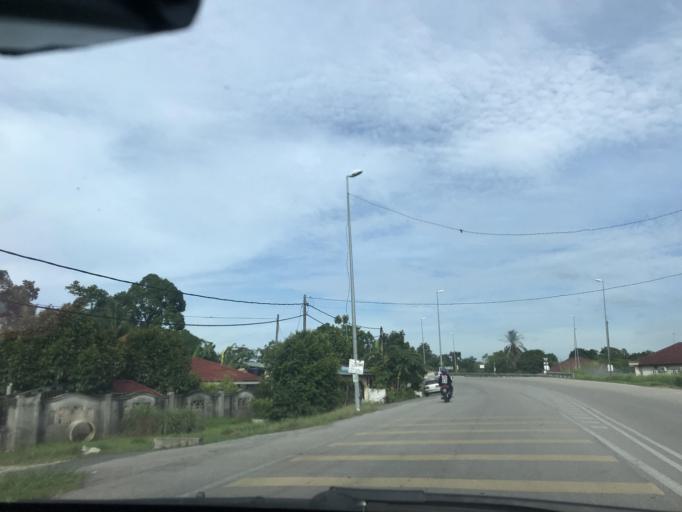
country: MY
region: Kelantan
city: Kota Bharu
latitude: 6.1391
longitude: 102.2043
